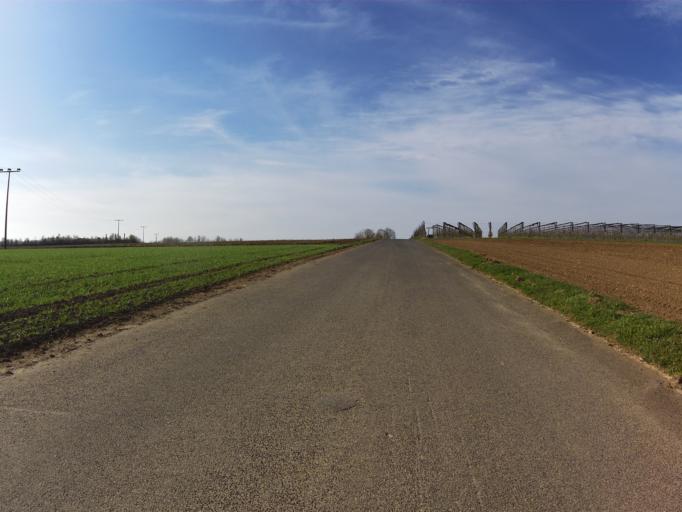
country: DE
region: Bavaria
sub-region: Regierungsbezirk Unterfranken
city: Biebelried
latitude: 49.7880
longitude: 10.1130
